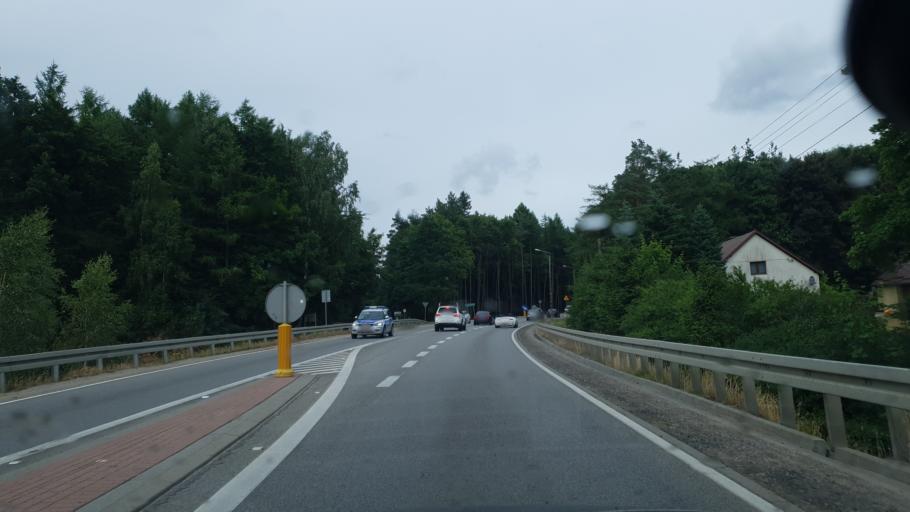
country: PL
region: Pomeranian Voivodeship
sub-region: Powiat kartuski
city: Chwaszczyno
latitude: 54.4305
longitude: 18.3914
